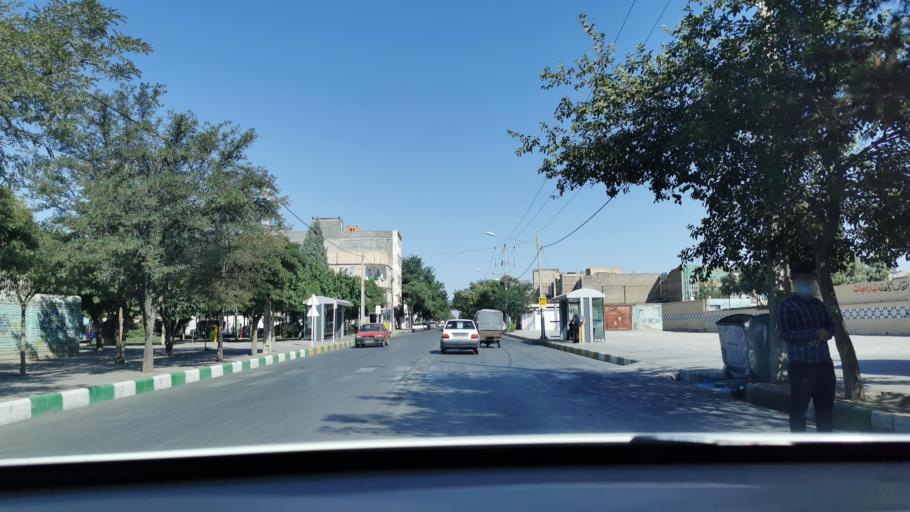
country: IR
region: Razavi Khorasan
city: Mashhad
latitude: 36.3345
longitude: 59.6389
